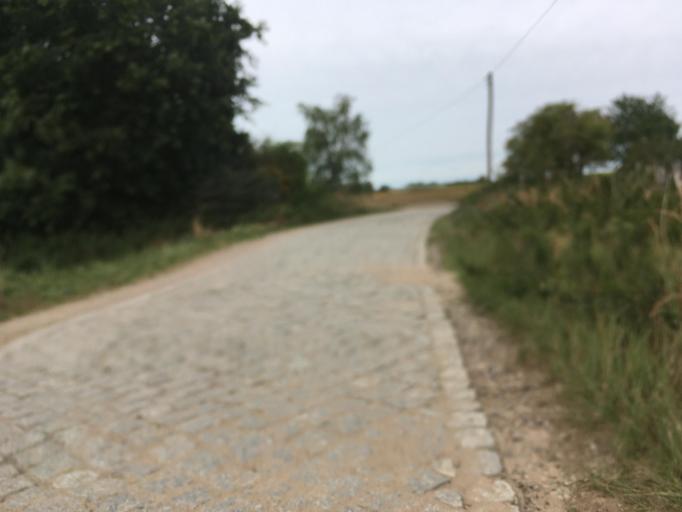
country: DE
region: Brandenburg
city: Gerswalde
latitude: 53.1828
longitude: 13.8390
